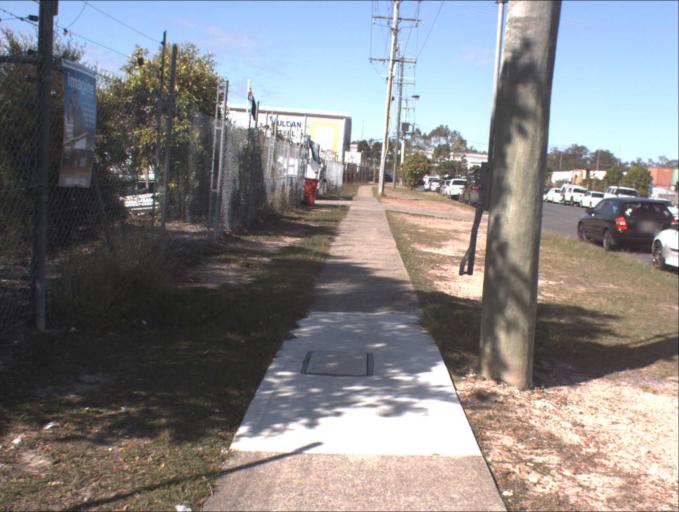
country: AU
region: Queensland
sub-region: Logan
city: Logan Reserve
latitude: -27.6863
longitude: 153.0777
